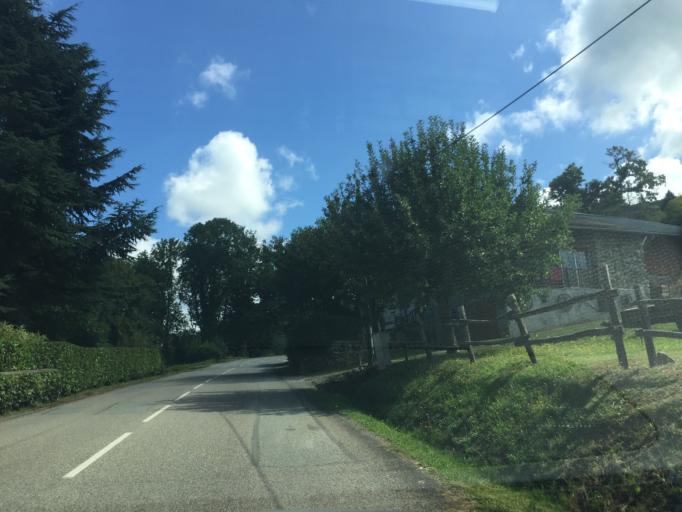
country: FR
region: Rhone-Alpes
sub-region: Departement de la Savoie
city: La Rochette
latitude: 45.4517
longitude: 6.1345
